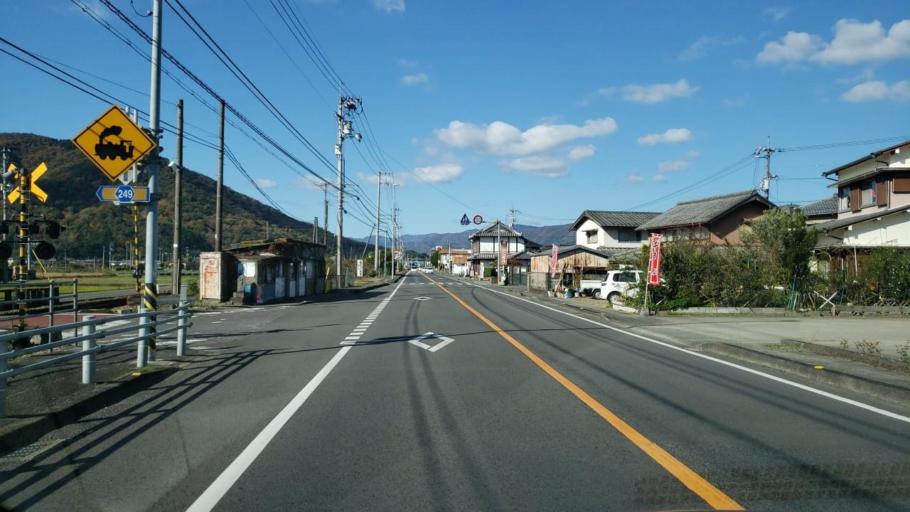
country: JP
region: Tokushima
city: Wakimachi
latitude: 34.0599
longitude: 134.2152
